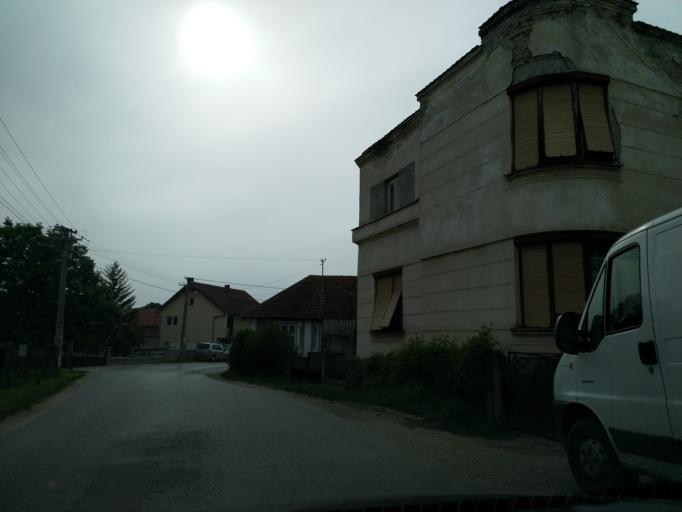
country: RS
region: Central Serbia
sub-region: Pomoravski Okrug
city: Jagodina
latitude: 43.9672
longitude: 21.2286
